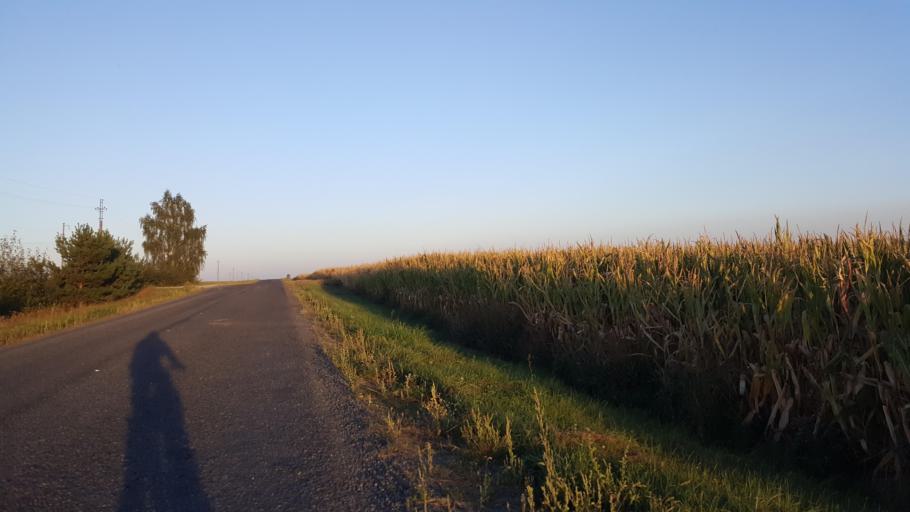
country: BY
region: Brest
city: Charnawchytsy
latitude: 52.2922
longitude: 23.5569
